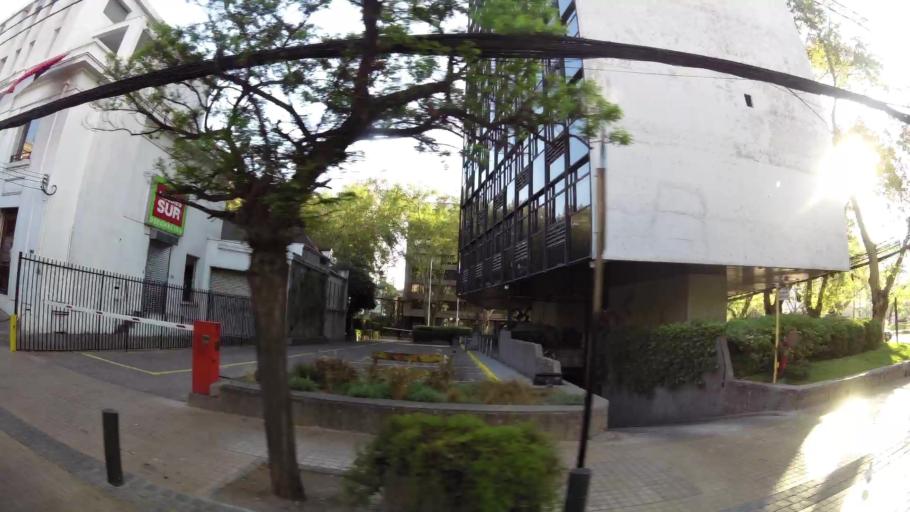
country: CL
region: Santiago Metropolitan
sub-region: Provincia de Santiago
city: Santiago
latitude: -33.4219
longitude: -70.6134
